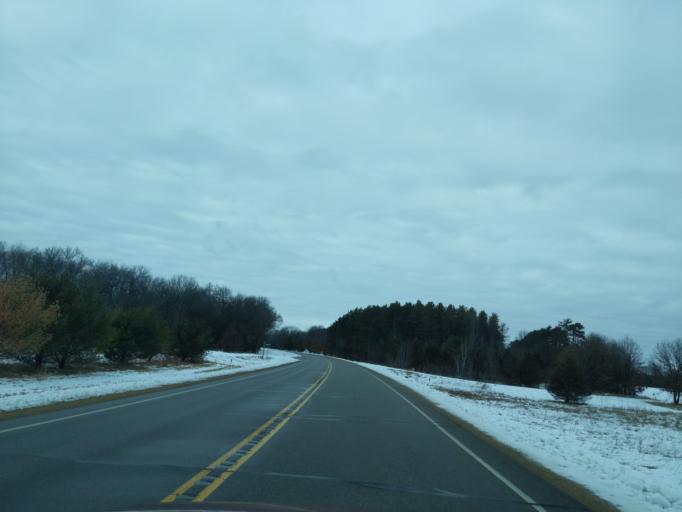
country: US
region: Wisconsin
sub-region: Waushara County
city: Wautoma
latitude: 43.9368
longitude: -89.3126
